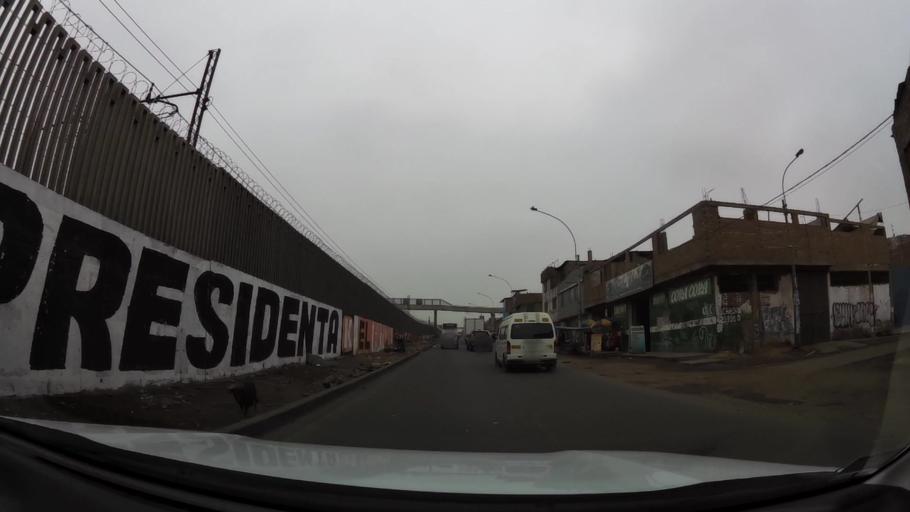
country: PE
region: Lima
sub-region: Lima
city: Surco
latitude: -12.1622
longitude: -76.9556
